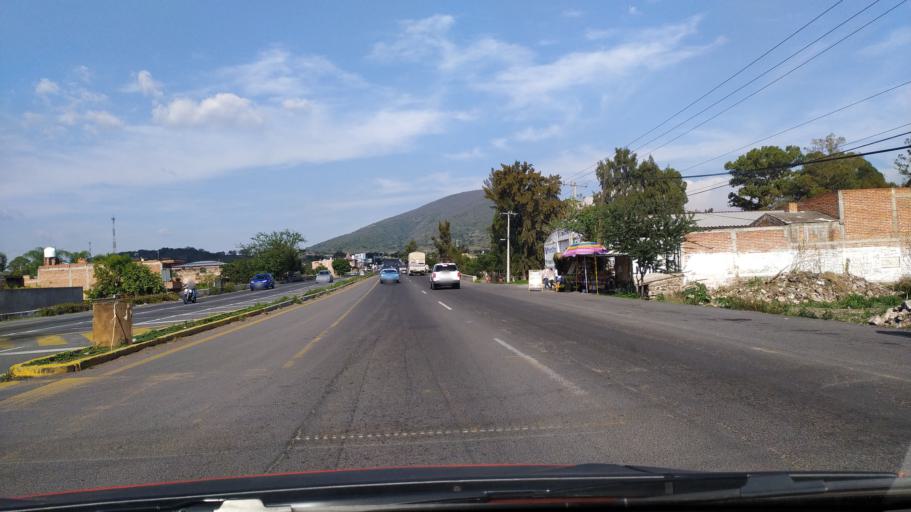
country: MX
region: Jalisco
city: Atotonilquillo
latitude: 20.3912
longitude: -103.1243
